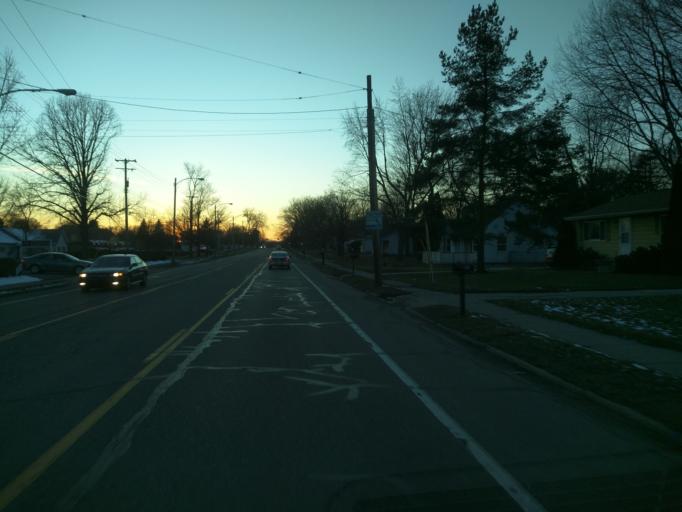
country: US
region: Michigan
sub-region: Ingham County
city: Lansing
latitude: 42.6976
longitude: -84.5863
